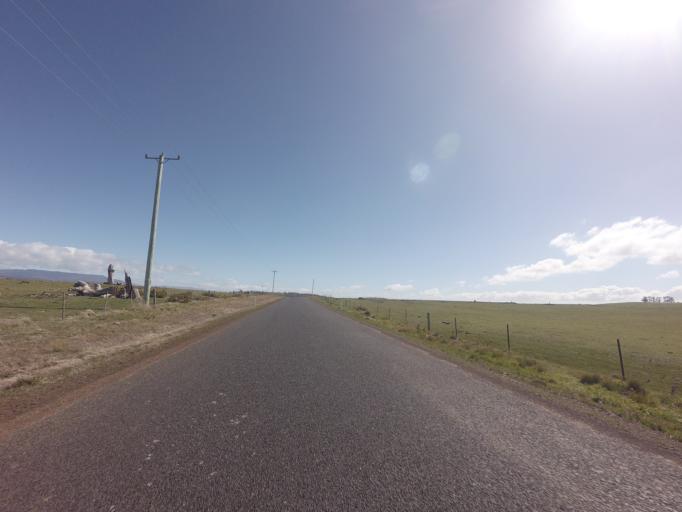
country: AU
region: Tasmania
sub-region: Northern Midlands
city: Evandale
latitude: -41.9018
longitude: 147.4461
